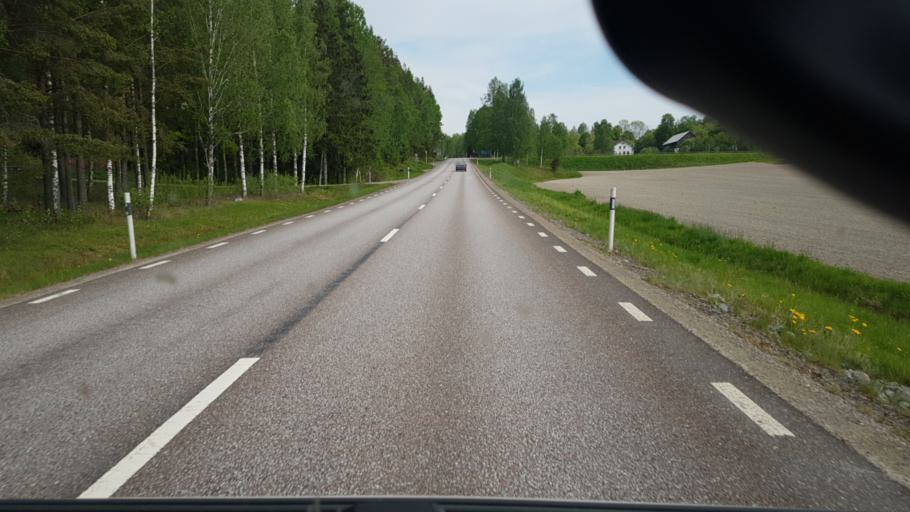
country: SE
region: Vaermland
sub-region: Arvika Kommun
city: Arvika
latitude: 59.4694
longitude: 12.7735
